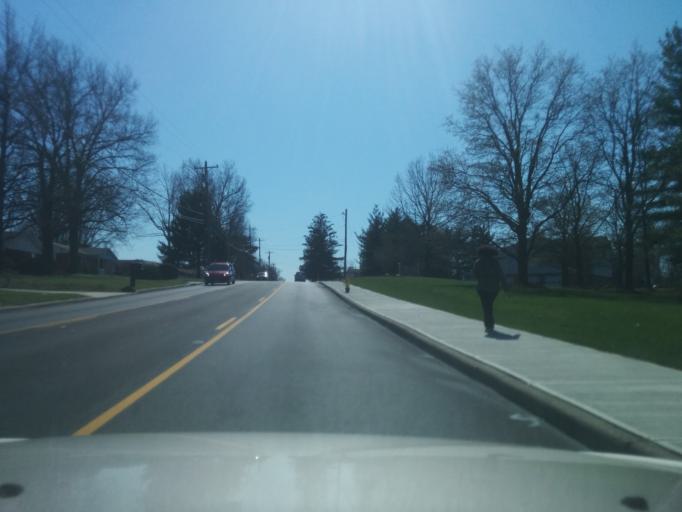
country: US
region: Ohio
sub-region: Hamilton County
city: White Oak
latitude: 39.2192
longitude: -84.6009
